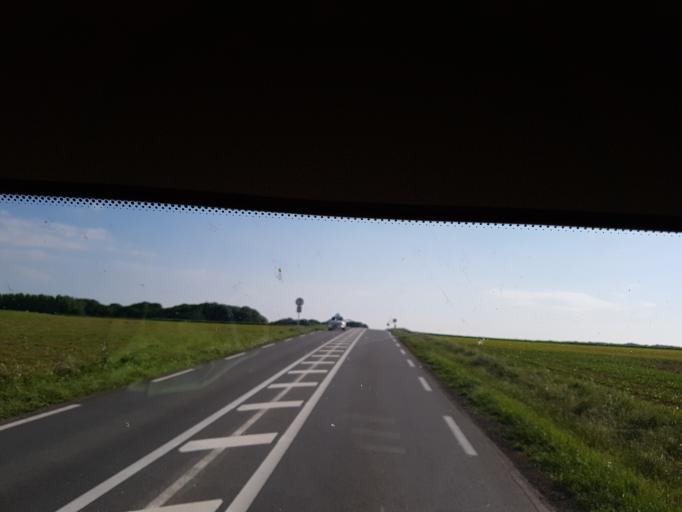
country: FR
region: Picardie
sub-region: Departement de la Somme
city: Crecy-en-Ponthieu
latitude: 50.2227
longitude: 1.9245
